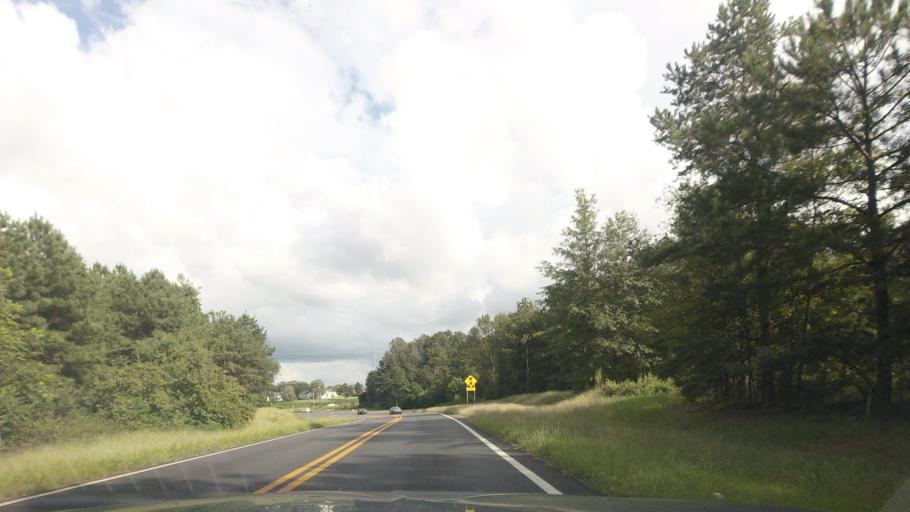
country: US
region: Georgia
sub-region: Houston County
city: Centerville
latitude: 32.6340
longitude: -83.7112
